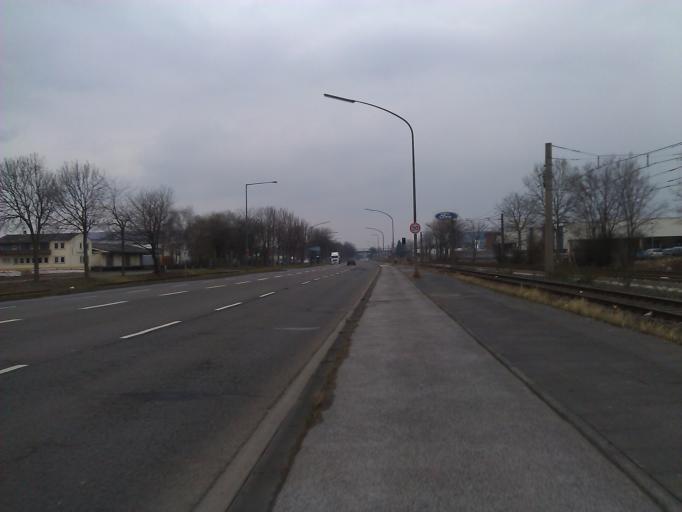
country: DE
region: North Rhine-Westphalia
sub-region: Regierungsbezirk Koln
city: Nippes
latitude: 51.0032
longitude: 6.9552
